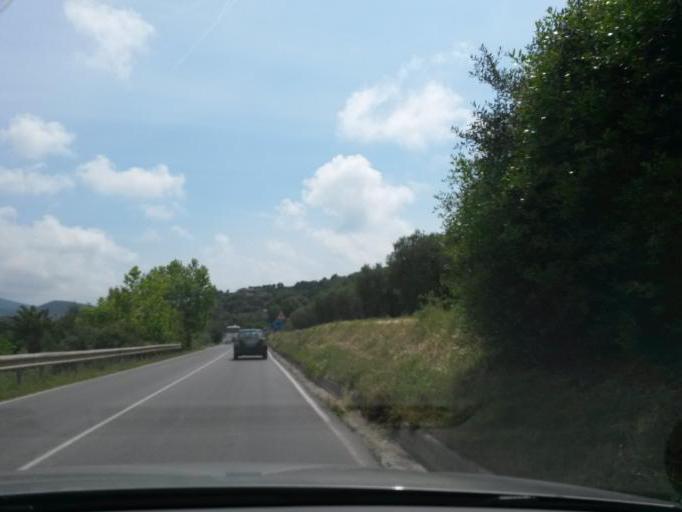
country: IT
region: Tuscany
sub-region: Provincia di Livorno
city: Capoliveri
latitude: 42.7752
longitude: 10.3505
